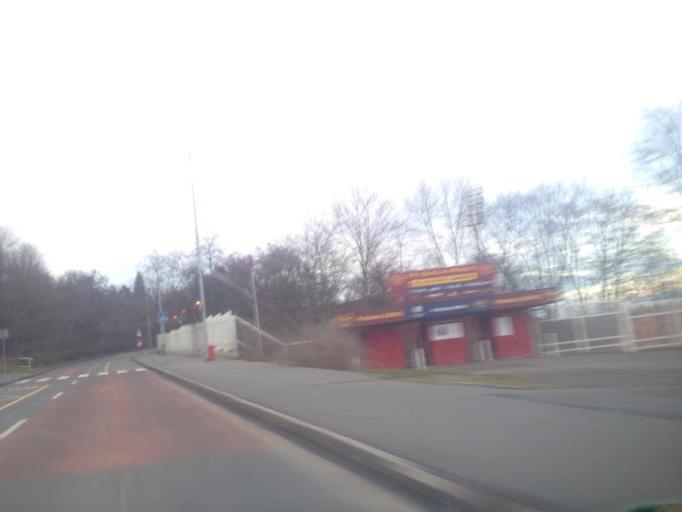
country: CZ
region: Praha
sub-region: Praha 1
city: Mala Strana
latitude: 50.1101
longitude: 14.3863
